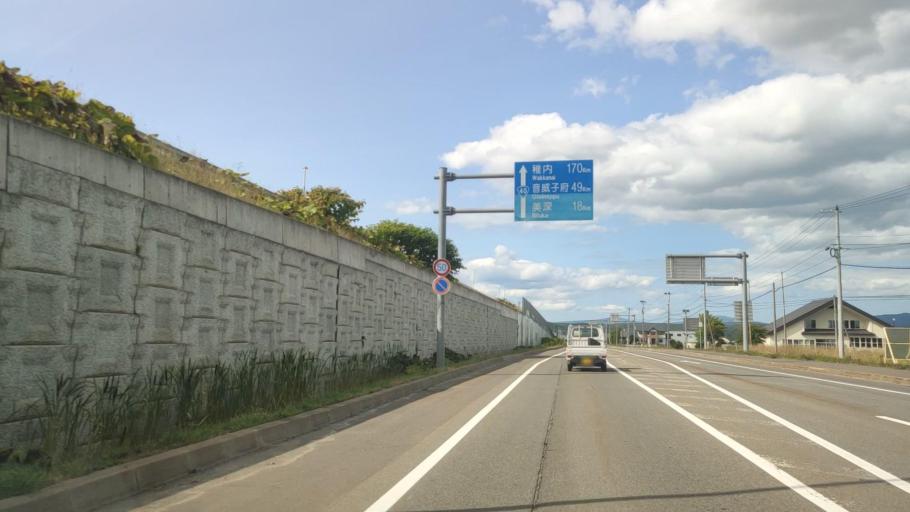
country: JP
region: Hokkaido
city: Nayoro
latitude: 44.3620
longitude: 142.4361
